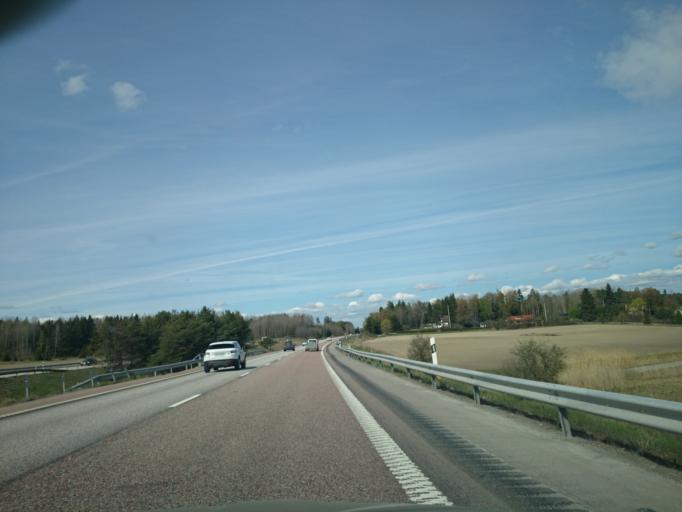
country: SE
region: Uppsala
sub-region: Uppsala Kommun
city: Alsike
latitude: 59.7776
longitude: 17.7820
